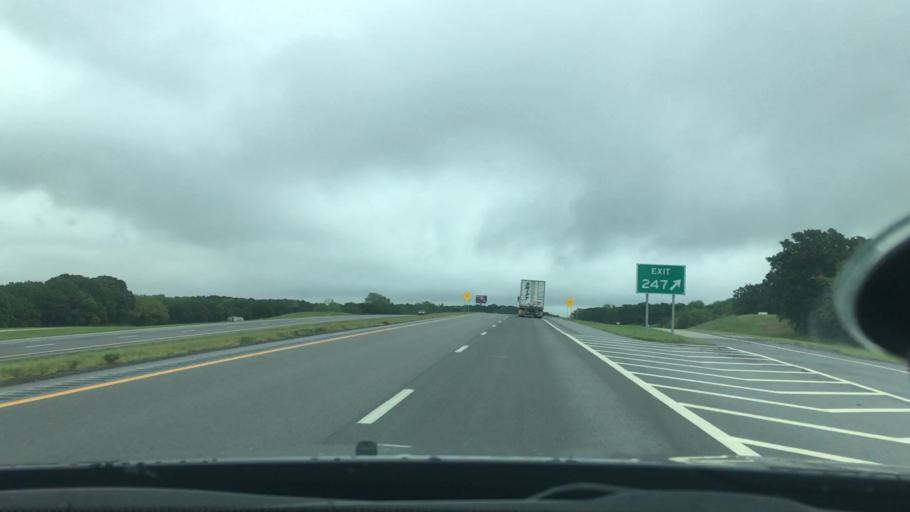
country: US
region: Oklahoma
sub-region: Okmulgee County
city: Henryetta
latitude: 35.4338
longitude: -95.8443
